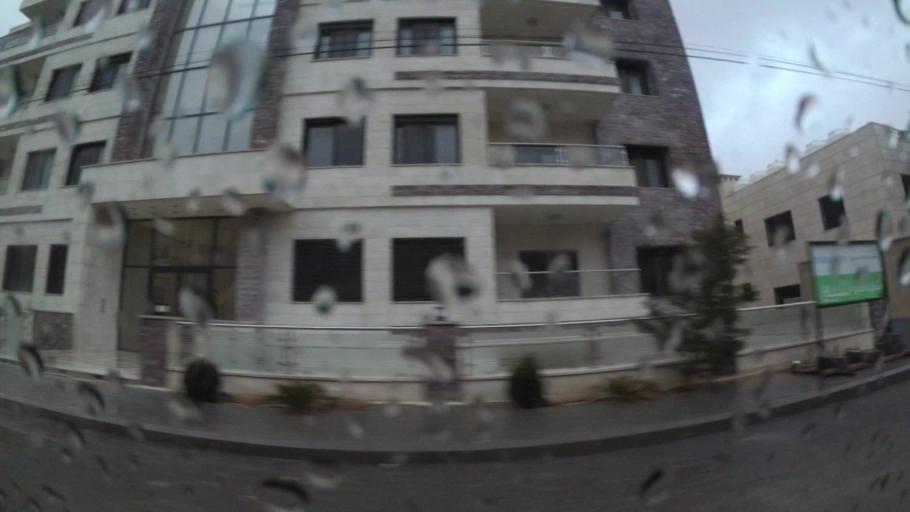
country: JO
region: Amman
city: Al Jubayhah
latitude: 32.0314
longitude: 35.8475
